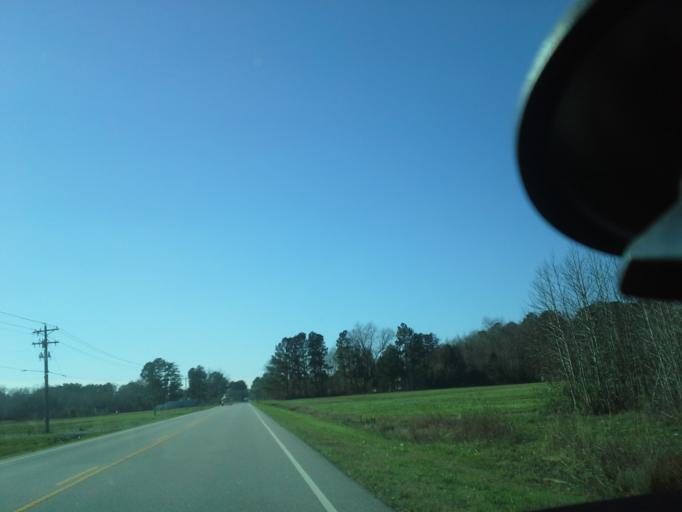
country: US
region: North Carolina
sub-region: Beaufort County
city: Belhaven
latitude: 35.5353
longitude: -76.7212
